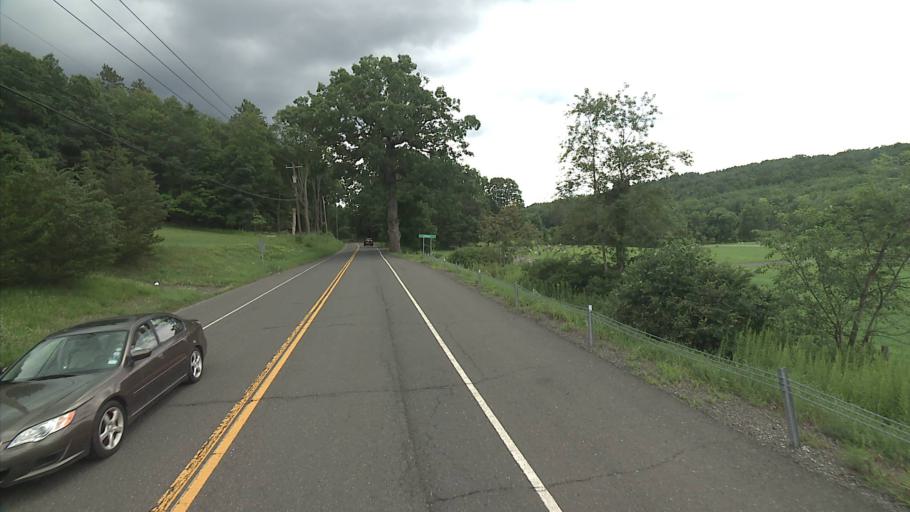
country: US
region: Connecticut
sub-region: Litchfield County
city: New Milford
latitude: 41.5658
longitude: -73.3141
